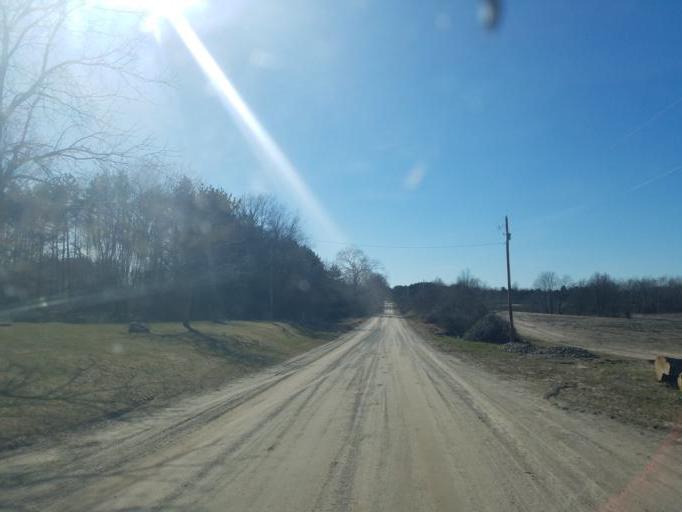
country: US
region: Michigan
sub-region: Isabella County
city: Lake Isabella
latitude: 43.5525
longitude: -85.0778
